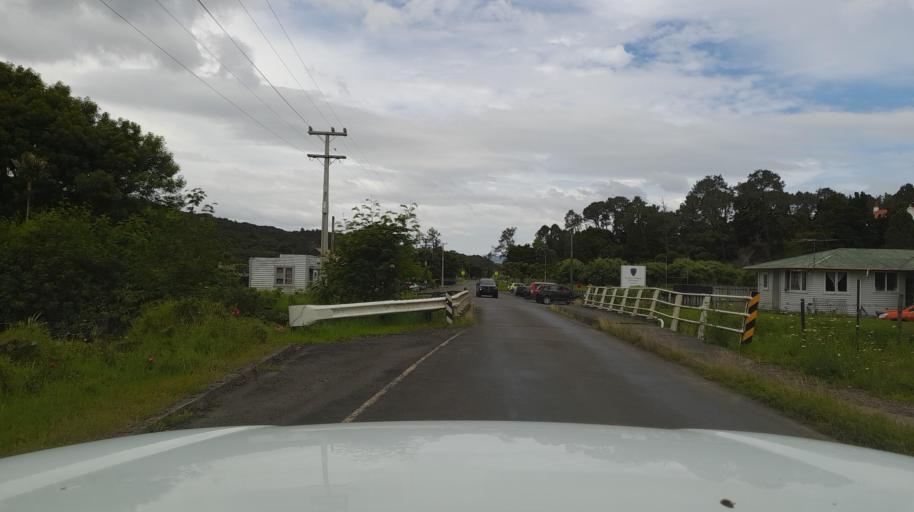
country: NZ
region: Northland
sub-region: Far North District
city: Kaitaia
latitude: -35.3800
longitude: 173.3834
